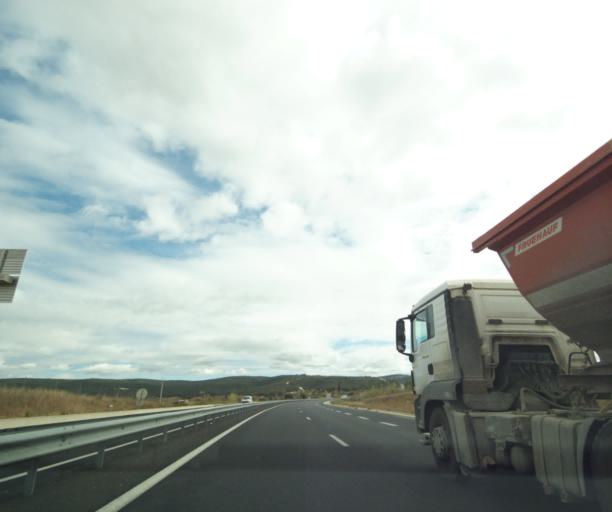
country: FR
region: Languedoc-Roussillon
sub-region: Departement de l'Herault
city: Gignac
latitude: 43.6396
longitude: 3.5767
